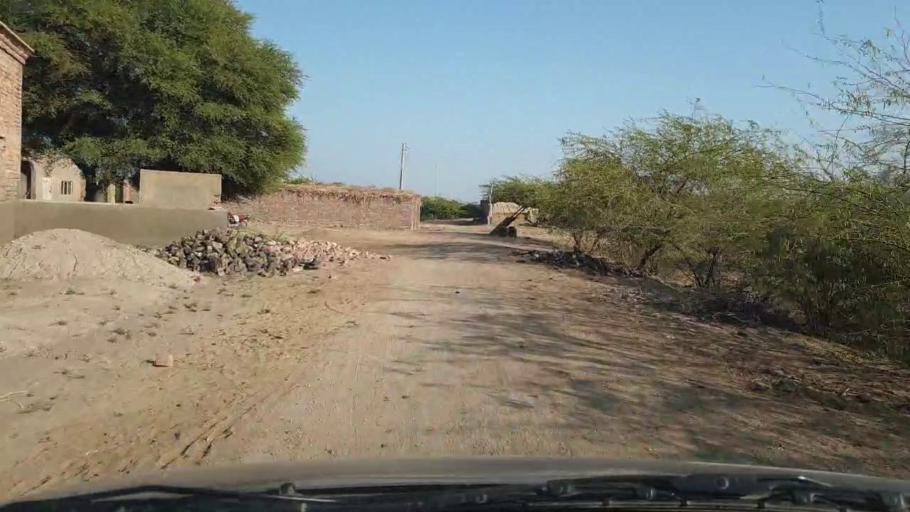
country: PK
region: Sindh
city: Samaro
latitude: 25.1437
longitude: 69.3065
